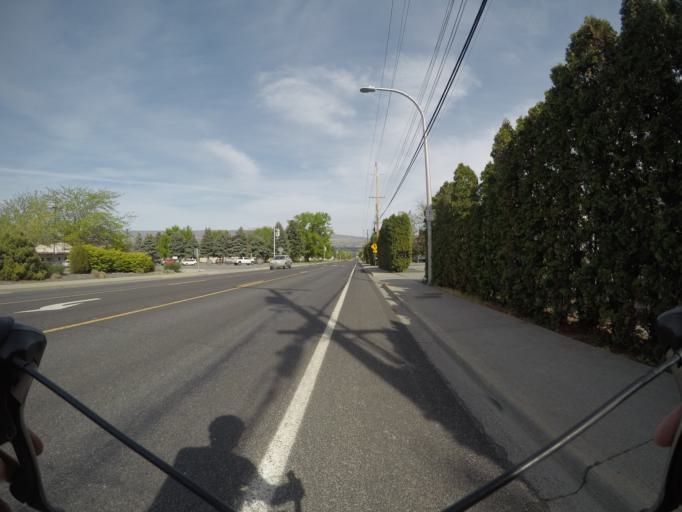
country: US
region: Washington
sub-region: Chelan County
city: West Wenatchee
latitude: 47.4298
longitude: -120.3394
